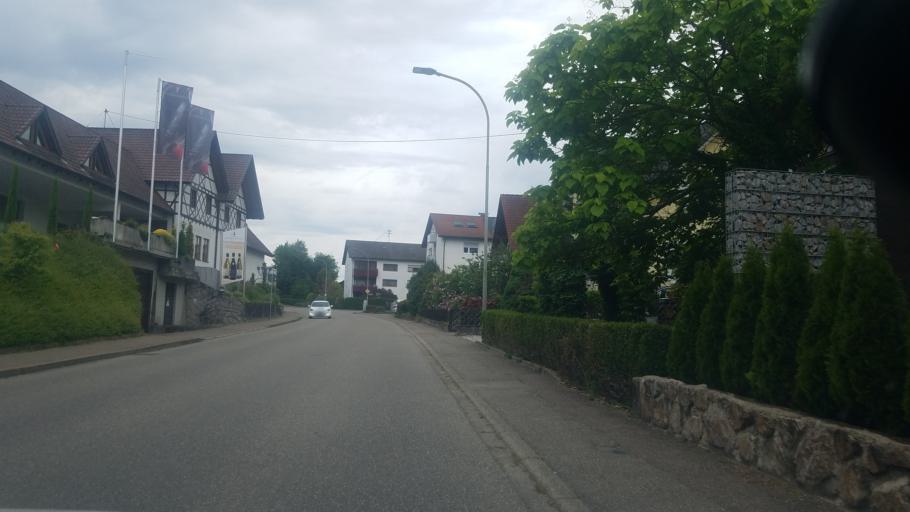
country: DE
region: Baden-Wuerttemberg
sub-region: Freiburg Region
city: Kappelrodeck
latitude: 48.5910
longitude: 8.1130
